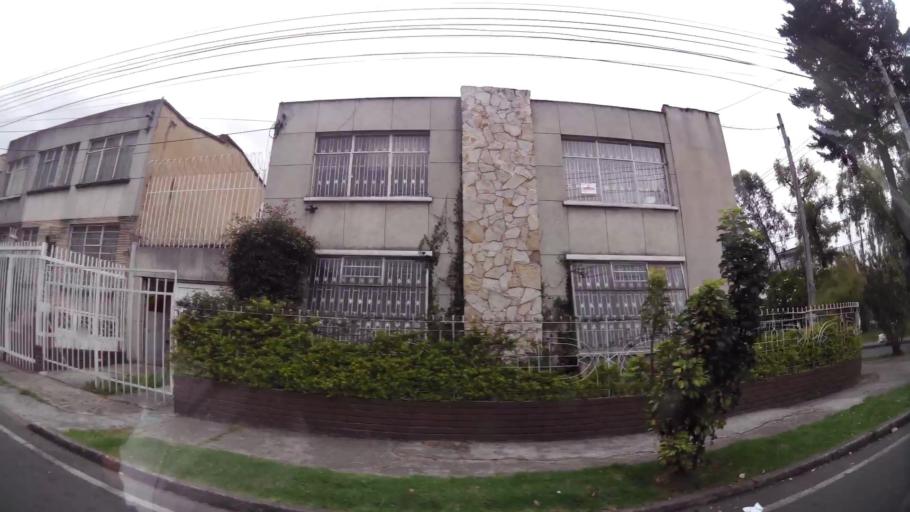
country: CO
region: Bogota D.C.
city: Bogota
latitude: 4.6274
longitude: -74.0795
